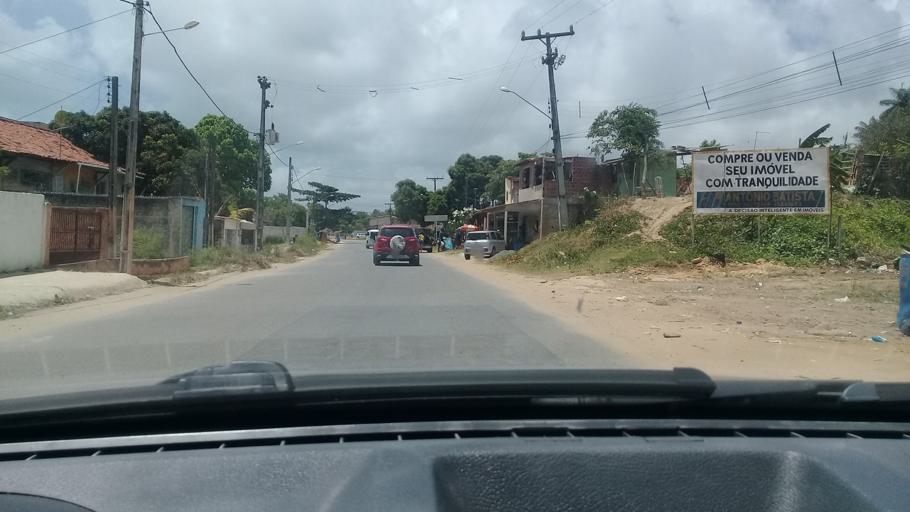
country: BR
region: Pernambuco
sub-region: Itamaraca
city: Itamaraca
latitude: -7.7938
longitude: -34.8418
